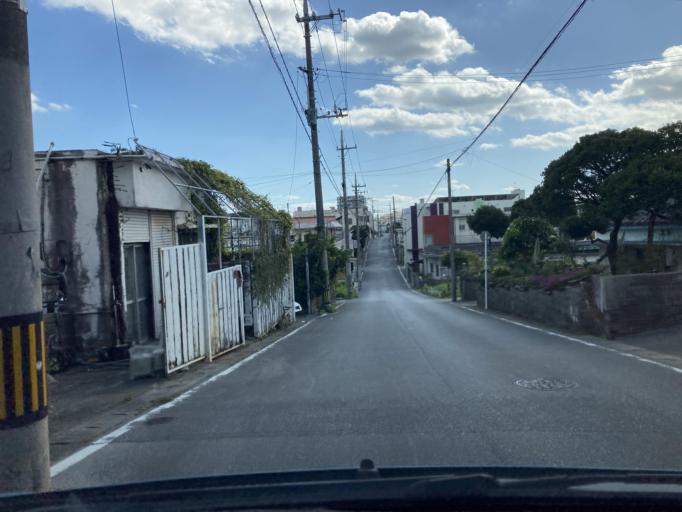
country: JP
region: Okinawa
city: Okinawa
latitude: 26.3420
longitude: 127.8060
